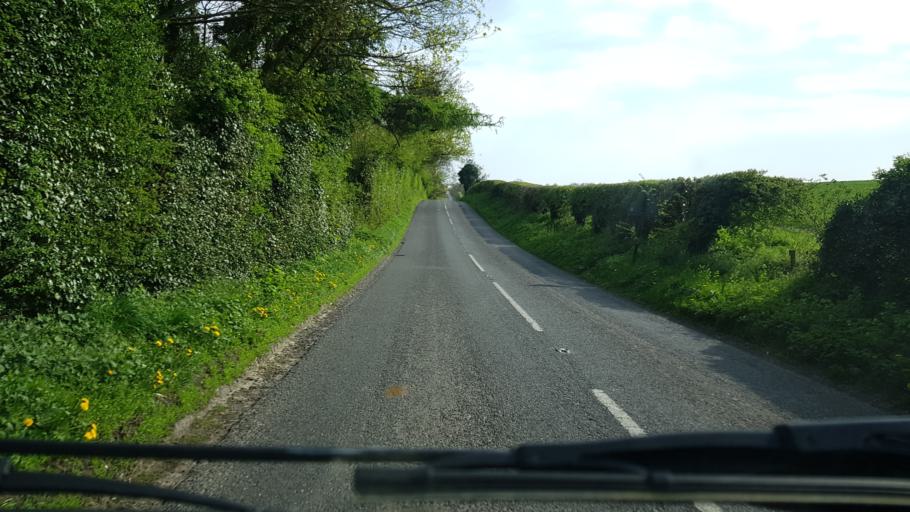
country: GB
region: England
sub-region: Hampshire
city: Overton
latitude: 51.2822
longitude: -1.2627
